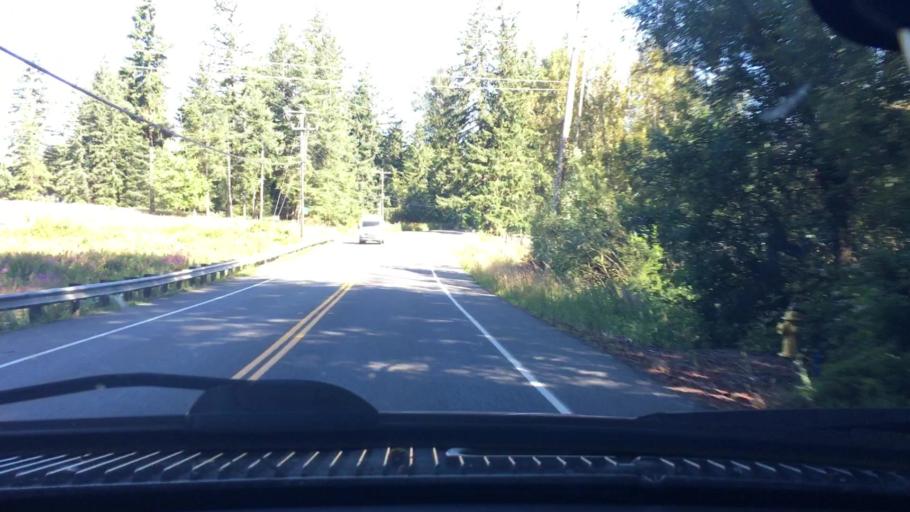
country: US
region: Washington
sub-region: King County
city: Lake Morton-Berrydale
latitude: 47.3308
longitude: -122.1197
